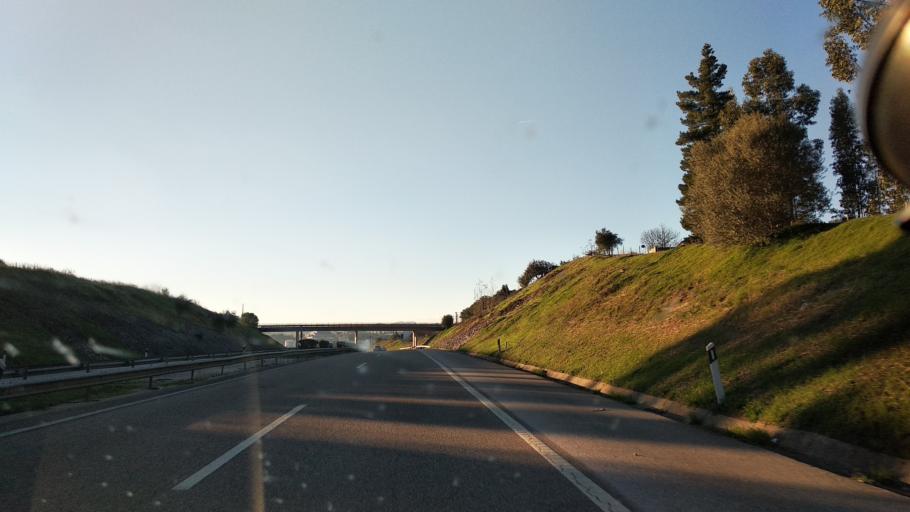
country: PT
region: Santarem
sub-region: Torres Novas
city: Riachos
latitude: 39.4690
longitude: -8.5123
